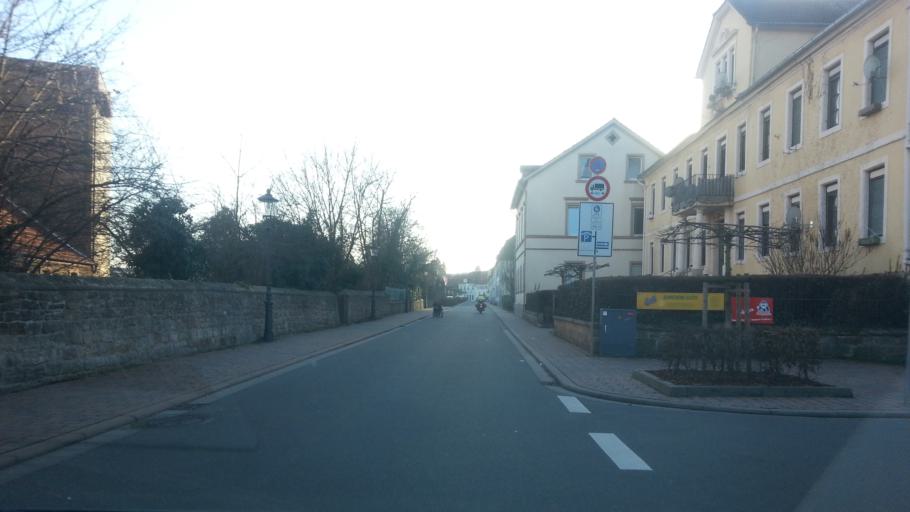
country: DE
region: Rheinland-Pfalz
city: Kirchheimbolanden
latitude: 49.6665
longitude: 8.0120
